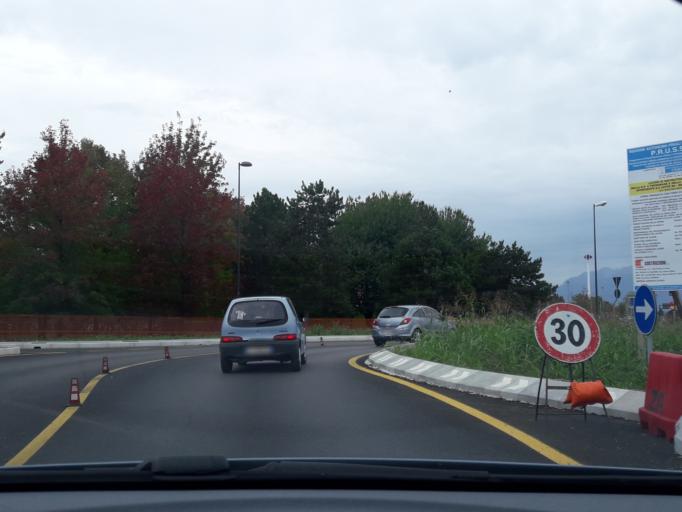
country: IT
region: Friuli Venezia Giulia
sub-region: Provincia di Udine
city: Tavagnacco
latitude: 46.1166
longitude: 13.2266
